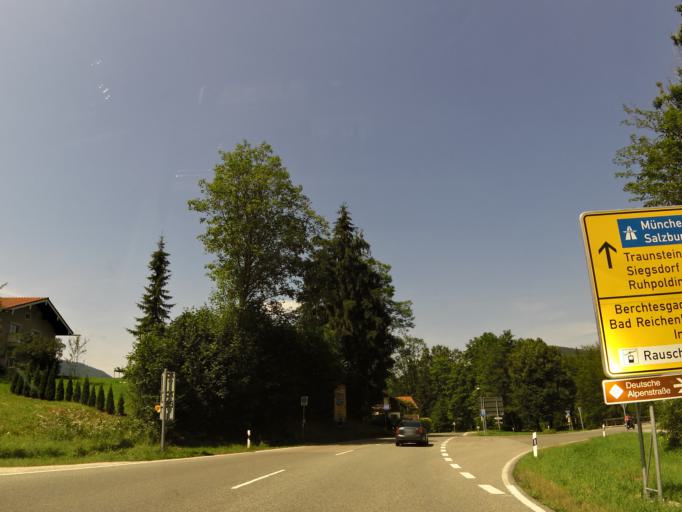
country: DE
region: Bavaria
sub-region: Upper Bavaria
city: Ruhpolding
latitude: 47.7395
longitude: 12.6588
